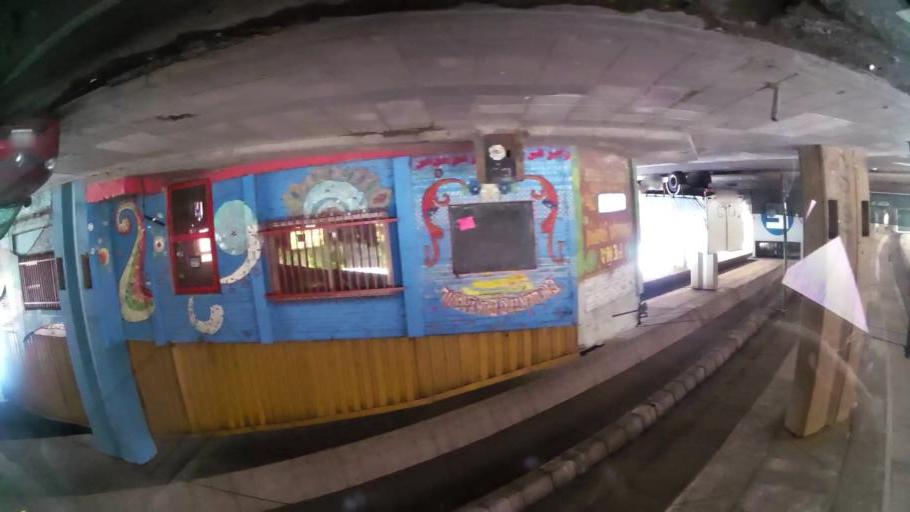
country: AR
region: Buenos Aires F.D.
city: Villa Santa Rita
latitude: -34.6363
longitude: -58.4497
